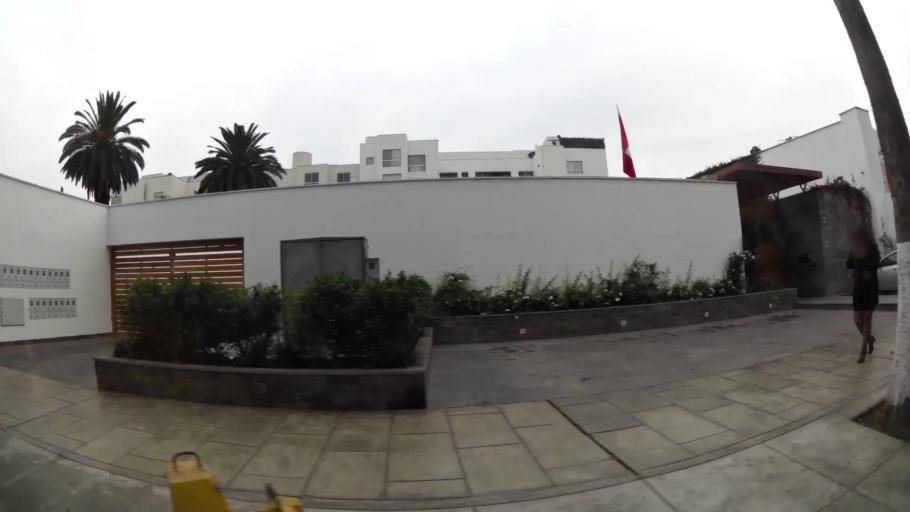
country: PE
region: Lima
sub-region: Lima
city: Surco
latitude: -12.1473
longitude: -77.0235
